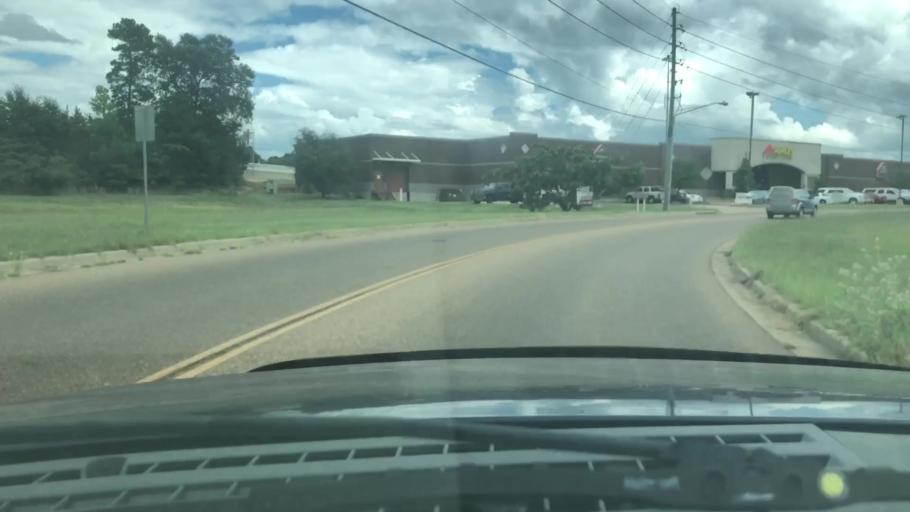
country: US
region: Texas
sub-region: Bowie County
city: Wake Village
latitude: 33.4494
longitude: -94.0991
